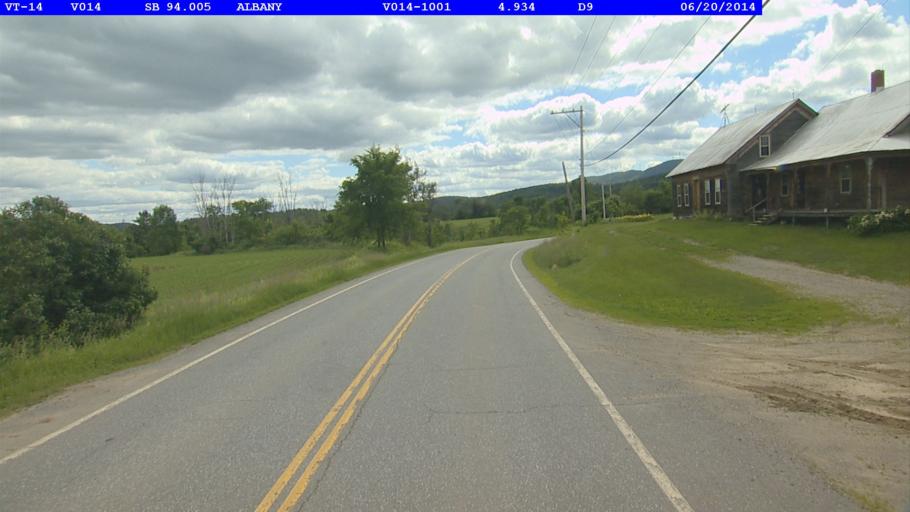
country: US
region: Vermont
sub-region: Orleans County
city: Newport
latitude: 44.7629
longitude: -72.3474
